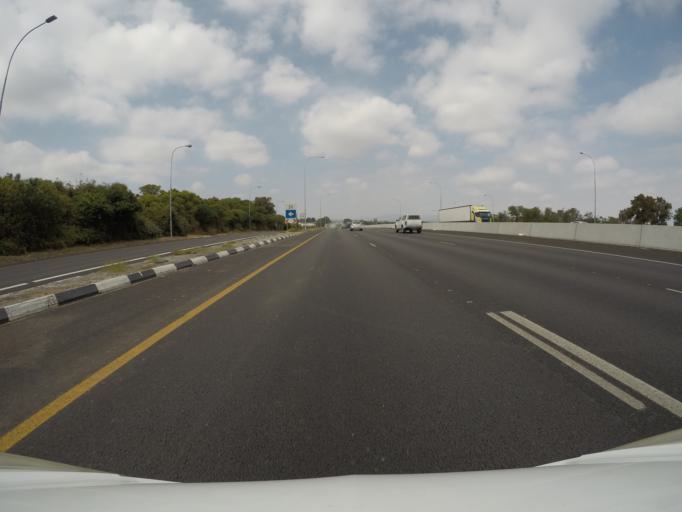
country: ZA
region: Western Cape
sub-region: City of Cape Town
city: Sunset Beach
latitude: -33.8895
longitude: 18.6054
